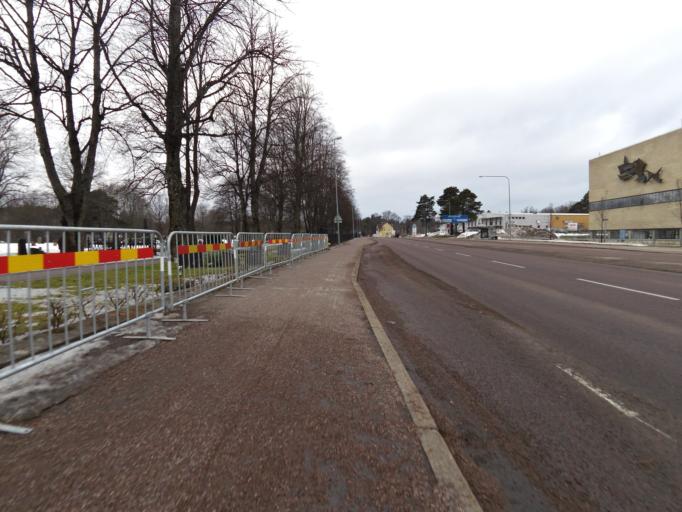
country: SE
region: Gaevleborg
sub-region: Gavle Kommun
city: Gavle
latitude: 60.6753
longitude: 17.1152
